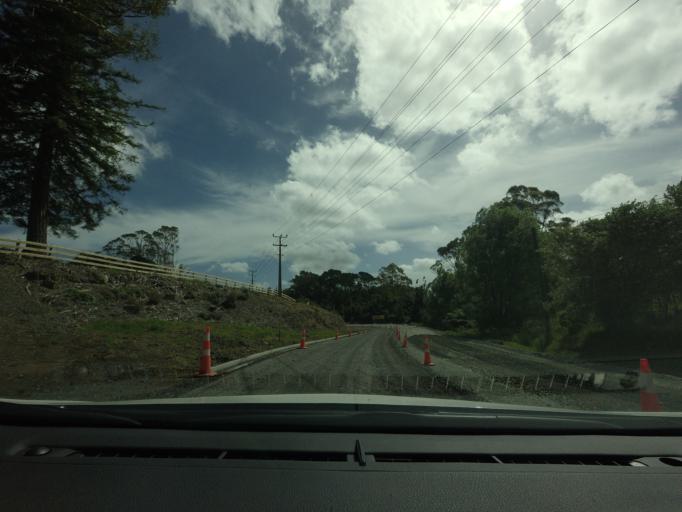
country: NZ
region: Auckland
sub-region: Auckland
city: Rothesay Bay
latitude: -36.7187
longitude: 174.6327
